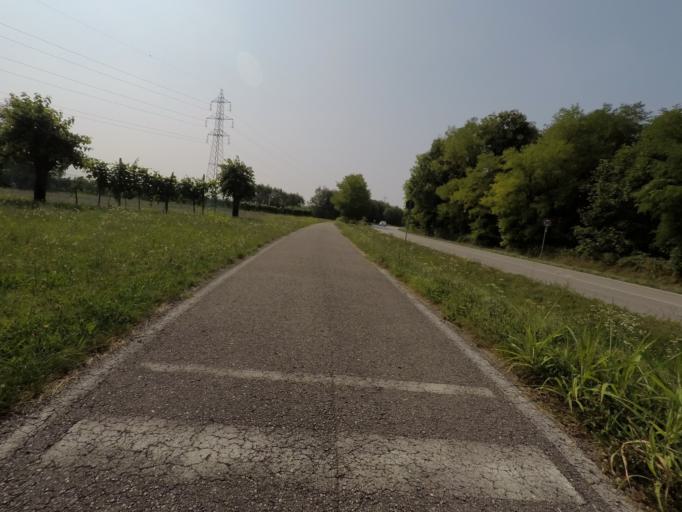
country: IT
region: Friuli Venezia Giulia
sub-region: Provincia di Pordenone
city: Maniago
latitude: 46.1674
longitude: 12.7213
